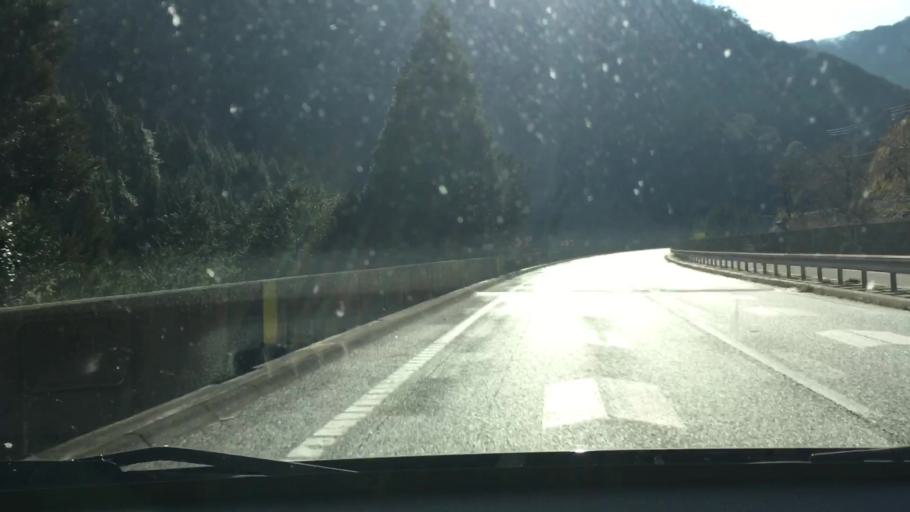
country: JP
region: Kumamoto
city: Hitoyoshi
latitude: 32.3188
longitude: 130.7564
